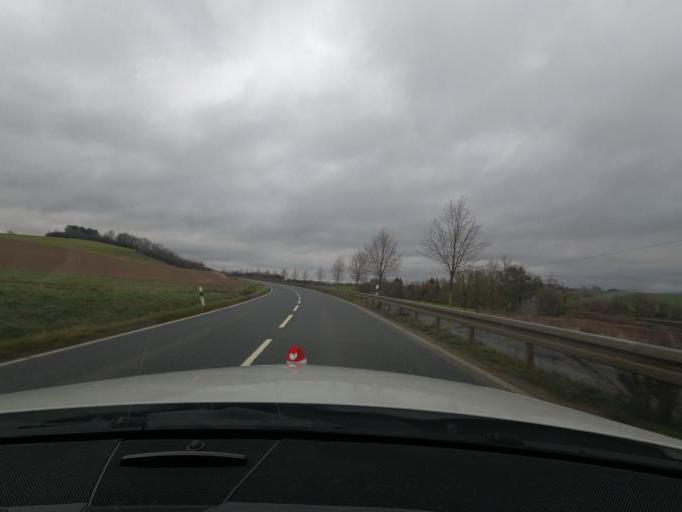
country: DE
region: Lower Saxony
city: Seesen
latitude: 51.8549
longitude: 10.1305
